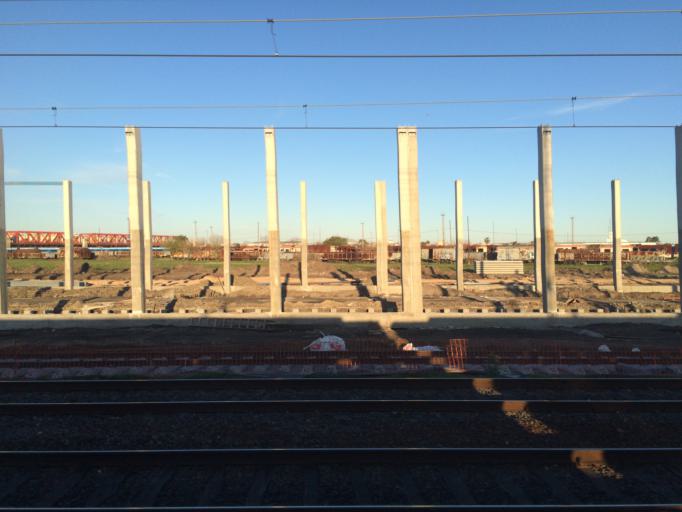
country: AR
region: Buenos Aires
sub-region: Partido de Avellaneda
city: Avellaneda
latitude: -34.6745
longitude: -58.3786
